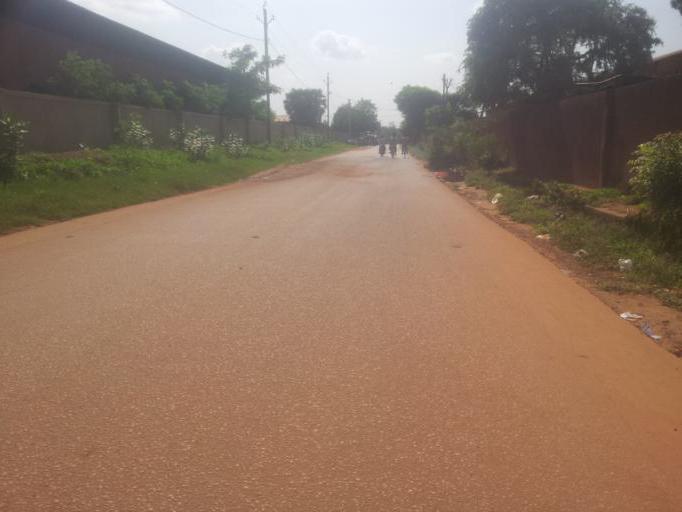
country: BF
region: Centre
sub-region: Kadiogo Province
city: Ouagadougou
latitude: 12.3625
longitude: -1.5418
